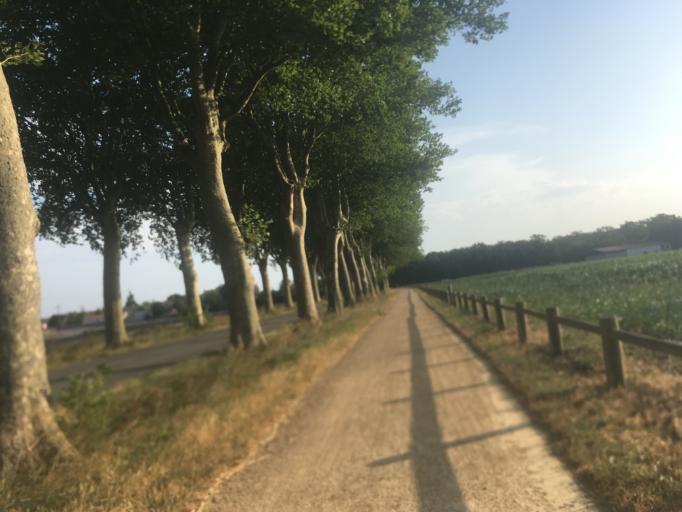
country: FR
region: Languedoc-Roussillon
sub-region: Departement de l'Aude
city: Bram
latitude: 43.2491
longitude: 2.1197
